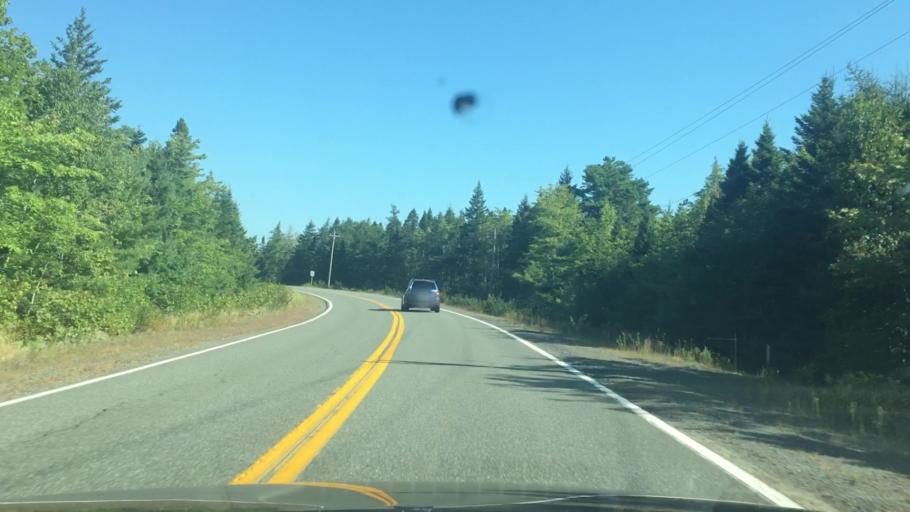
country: CA
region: Nova Scotia
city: Cole Harbour
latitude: 44.8014
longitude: -62.8807
